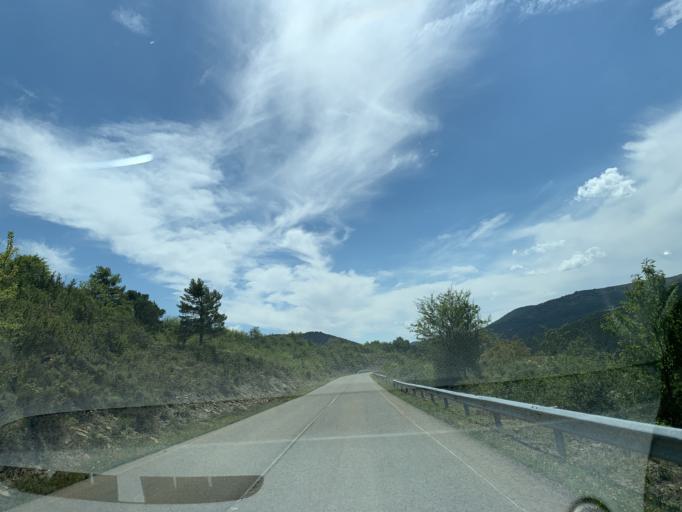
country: ES
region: Aragon
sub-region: Provincia de Huesca
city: Borau
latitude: 42.6650
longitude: -0.6252
